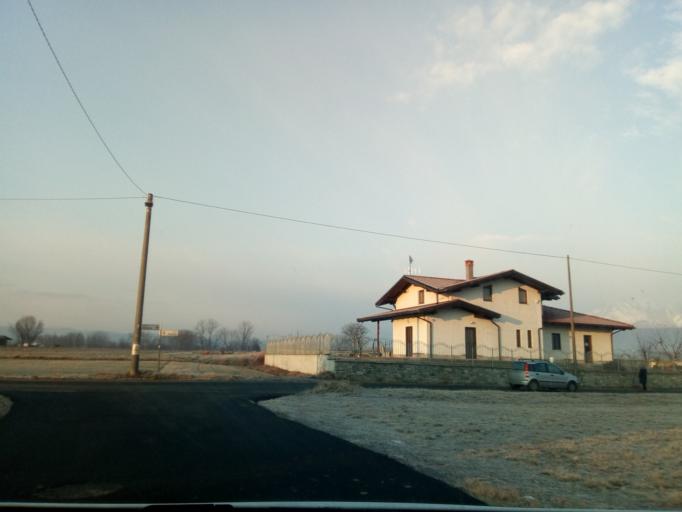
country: IT
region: Piedmont
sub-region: Provincia di Torino
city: Pavone Canavese
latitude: 45.4294
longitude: 7.8757
